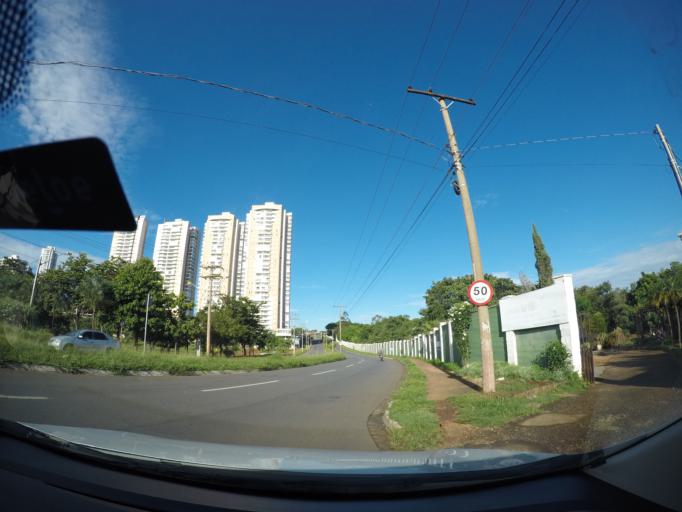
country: BR
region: Goias
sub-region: Goiania
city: Goiania
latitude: -16.7307
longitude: -49.2926
